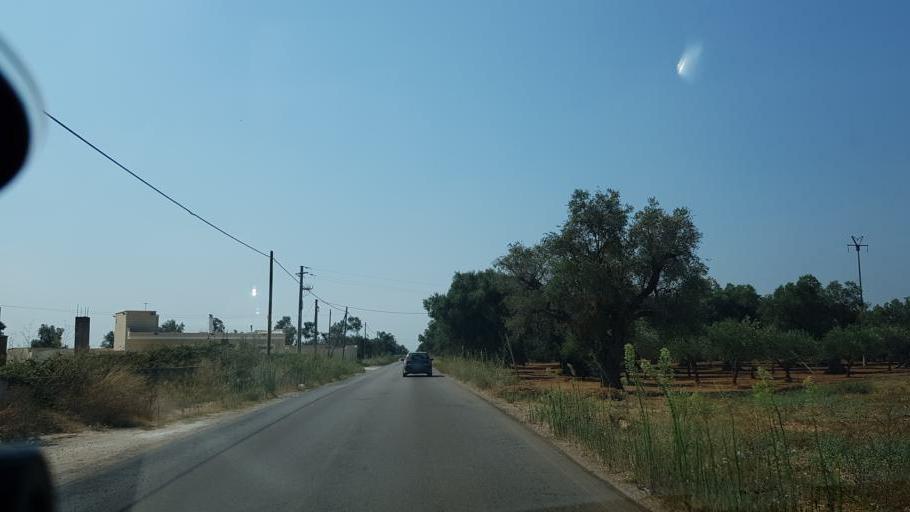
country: IT
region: Apulia
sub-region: Provincia di Taranto
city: Manduria
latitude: 40.4162
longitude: 17.6320
